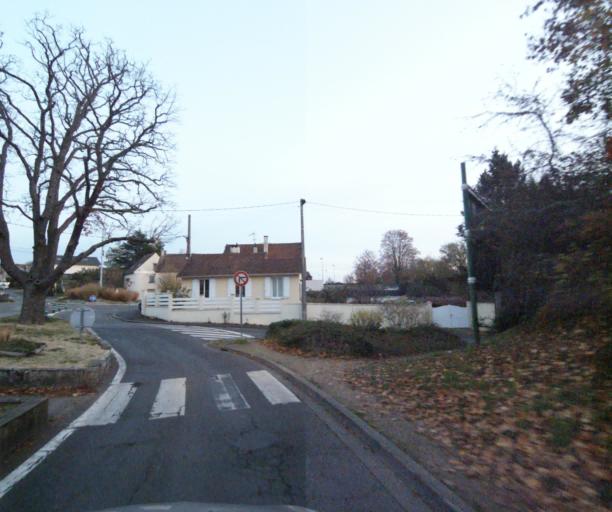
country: FR
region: Ile-de-France
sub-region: Departement des Yvelines
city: Triel-sur-Seine
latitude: 48.9760
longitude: 2.0100
